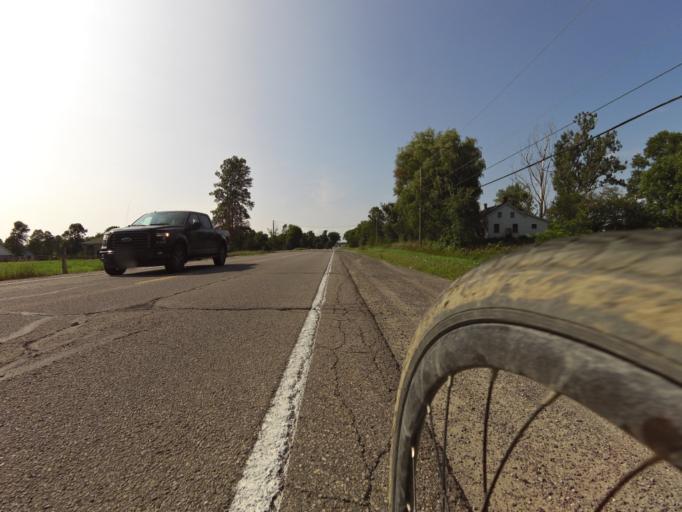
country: CA
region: Ontario
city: Kingston
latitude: 44.3523
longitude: -76.6426
